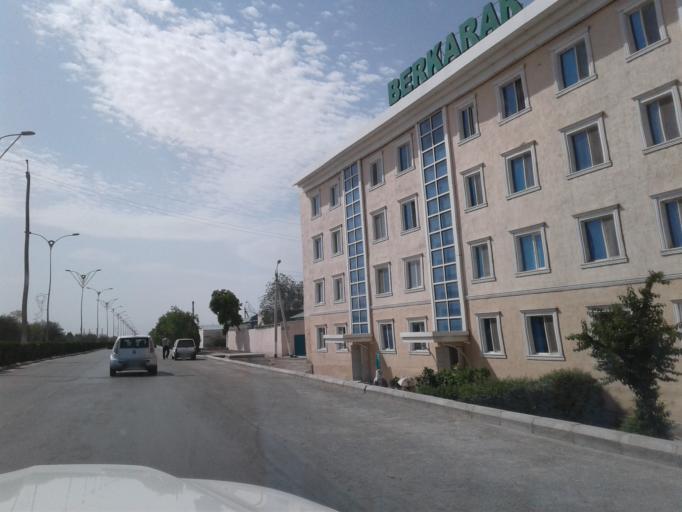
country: TM
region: Dasoguz
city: Dasoguz
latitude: 41.8301
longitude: 59.9444
